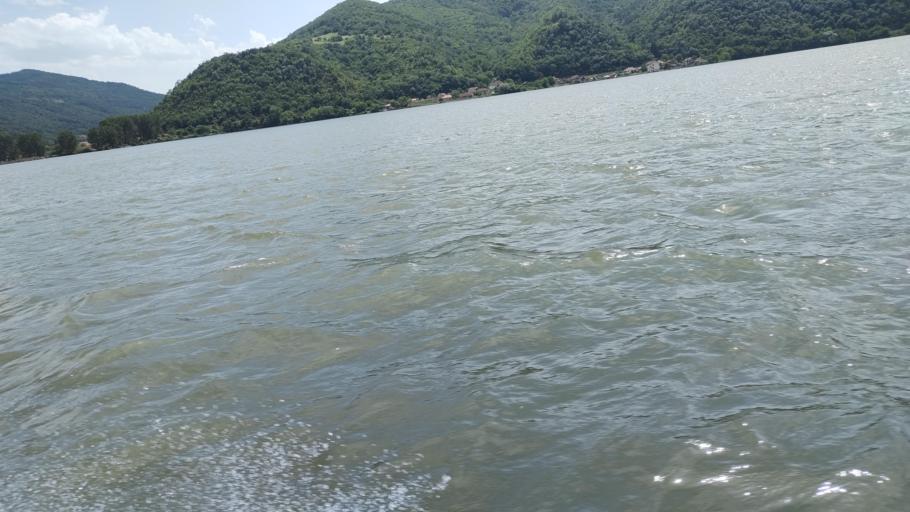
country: RO
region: Caras-Severin
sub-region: Comuna Berzasca
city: Liubcova
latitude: 44.6471
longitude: 21.9059
